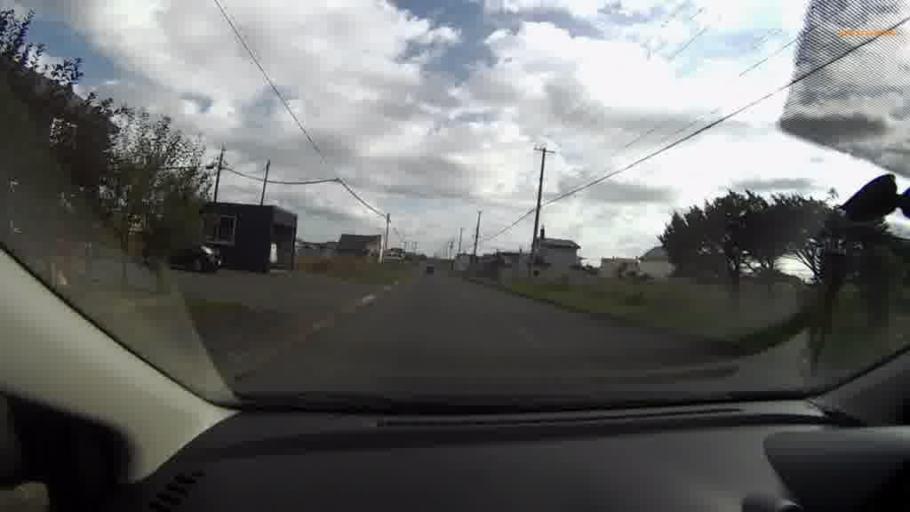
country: JP
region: Hokkaido
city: Kushiro
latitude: 42.9762
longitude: 144.1239
